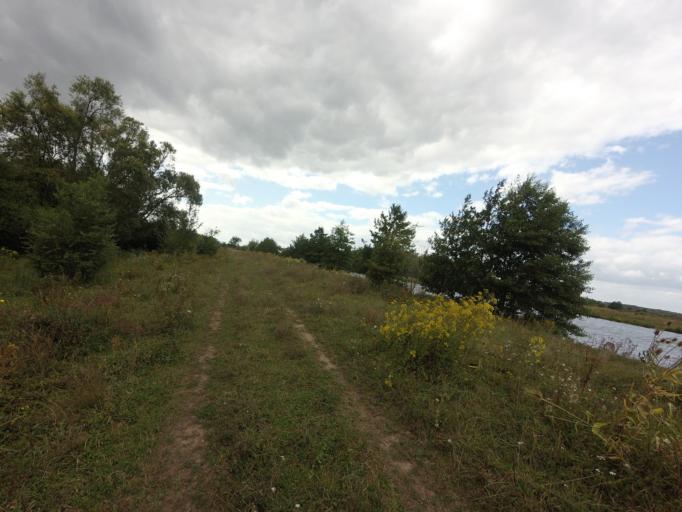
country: NL
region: Limburg
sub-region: Gemeente Maasgouw
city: Maasbracht
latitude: 51.1487
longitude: 5.8628
